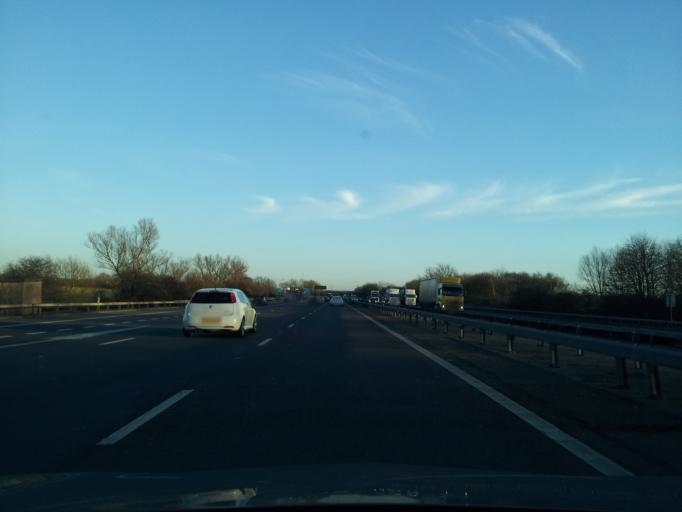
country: GB
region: England
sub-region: Milton Keynes
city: Broughton
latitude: 52.0619
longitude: -0.7072
